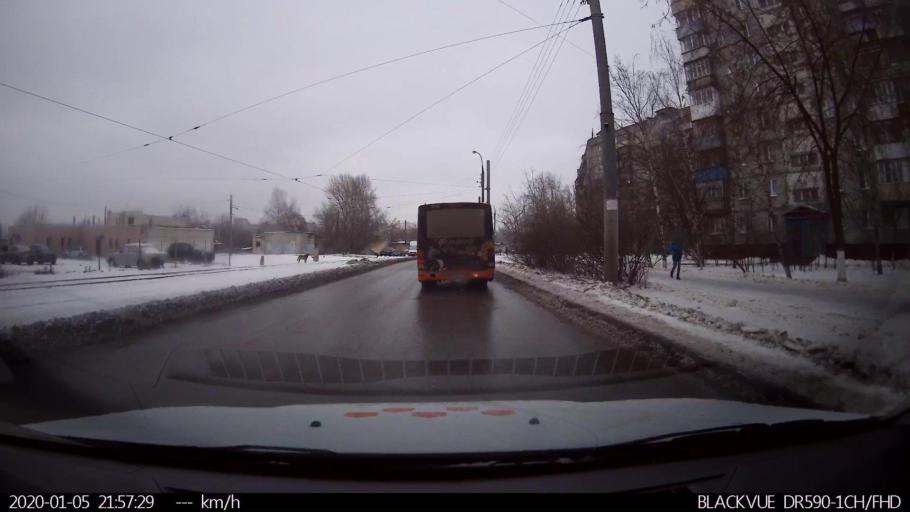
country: RU
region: Nizjnij Novgorod
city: Gorbatovka
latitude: 56.2651
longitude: 43.8521
